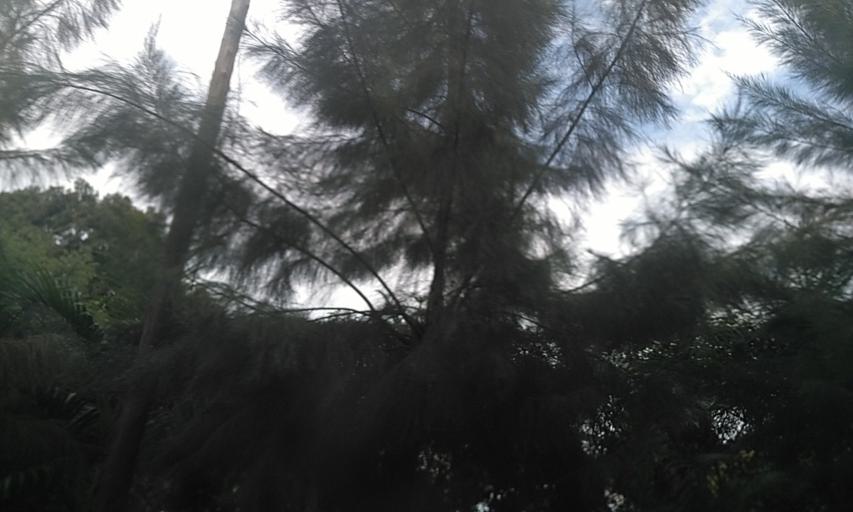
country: UG
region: Central Region
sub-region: Kampala District
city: Kampala
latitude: 0.3227
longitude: 32.5951
